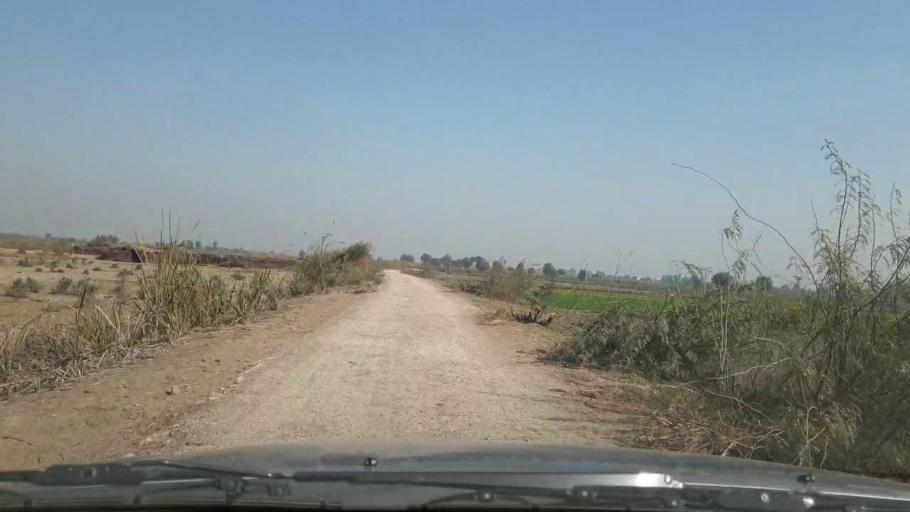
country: PK
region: Sindh
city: Mirpur Mathelo
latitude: 28.0381
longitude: 69.5546
